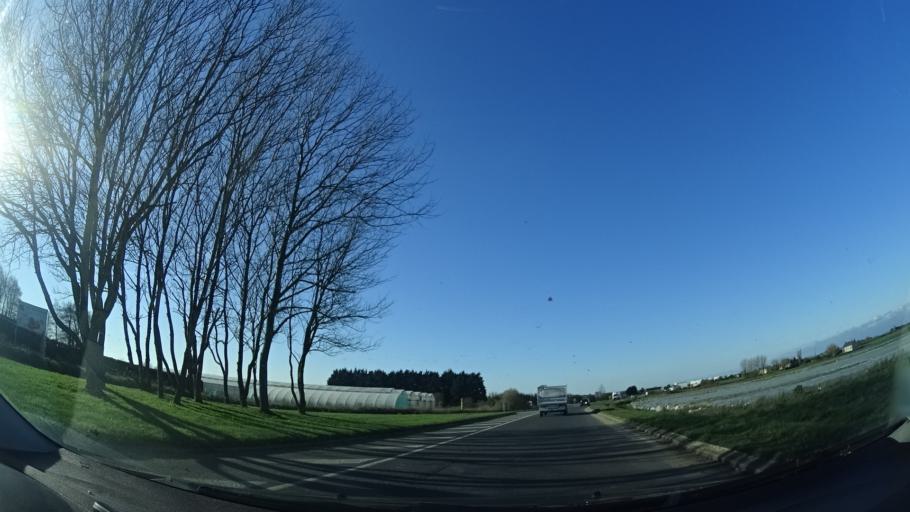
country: FR
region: Brittany
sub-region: Departement du Finistere
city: Saint-Pol-de-Leon
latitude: 48.6638
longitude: -3.9894
